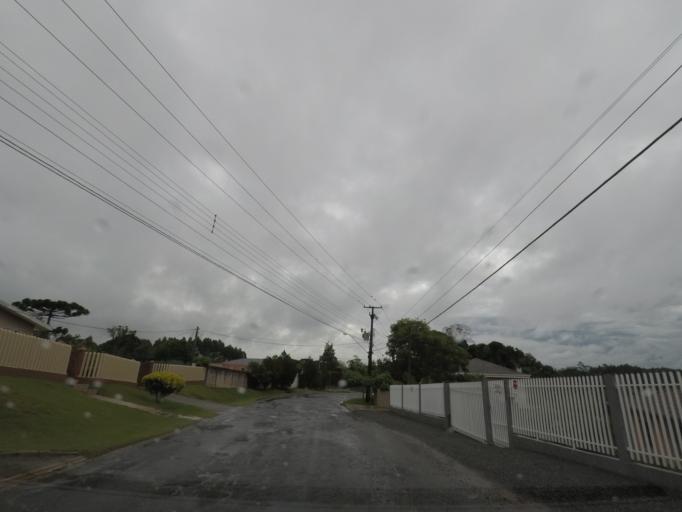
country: BR
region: Parana
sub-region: Campo Largo
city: Campo Largo
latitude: -25.4577
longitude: -49.4311
